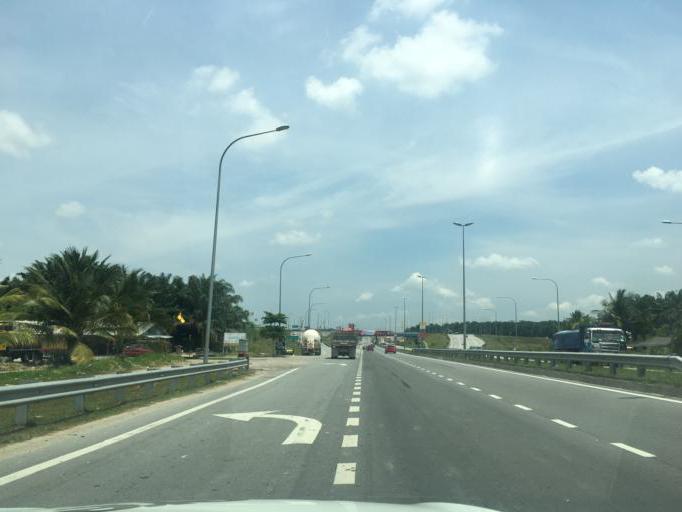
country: MY
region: Putrajaya
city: Putrajaya
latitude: 2.8540
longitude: 101.6948
